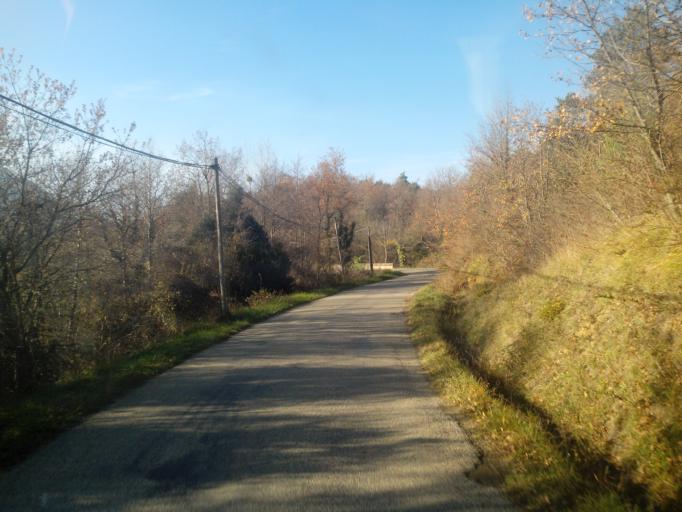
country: FR
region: Languedoc-Roussillon
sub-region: Departement des Pyrenees-Orientales
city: Saint-Paul-de-Fenouillet
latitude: 42.8618
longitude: 2.4408
